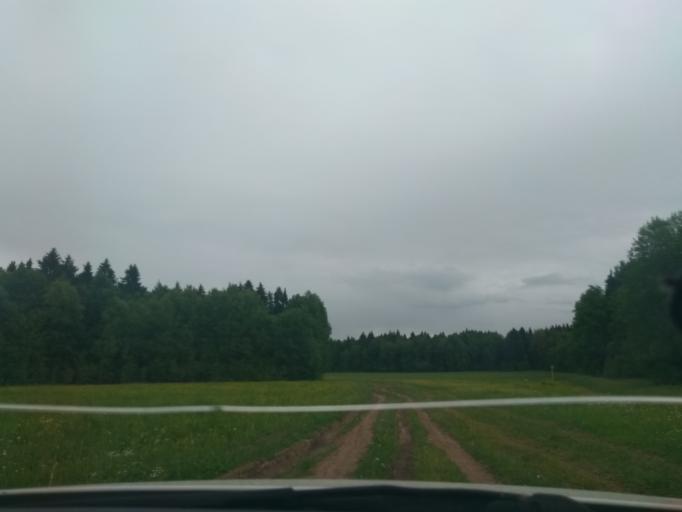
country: RU
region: Perm
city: Perm
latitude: 57.9841
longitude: 56.3310
